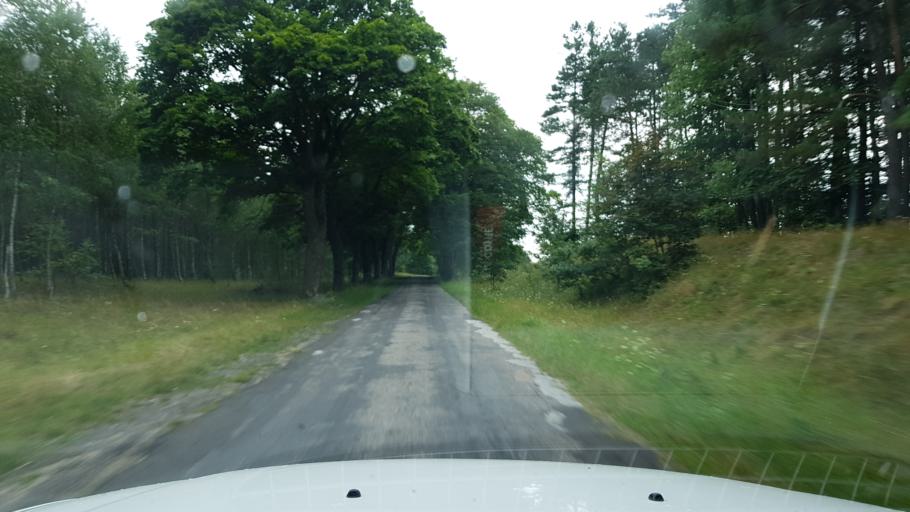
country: PL
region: West Pomeranian Voivodeship
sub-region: Powiat koszalinski
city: Bobolice
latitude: 53.9224
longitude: 16.6585
